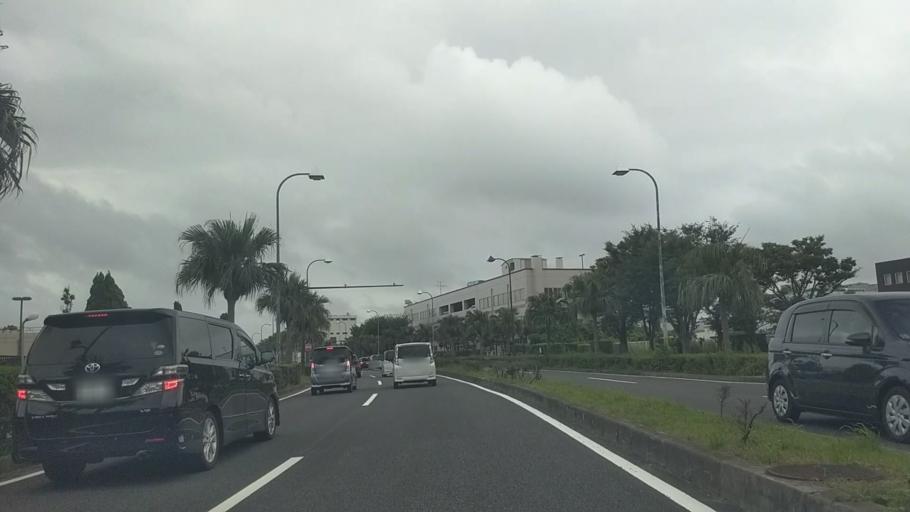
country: JP
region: Kanagawa
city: Yokosuka
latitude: 35.2710
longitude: 139.6848
